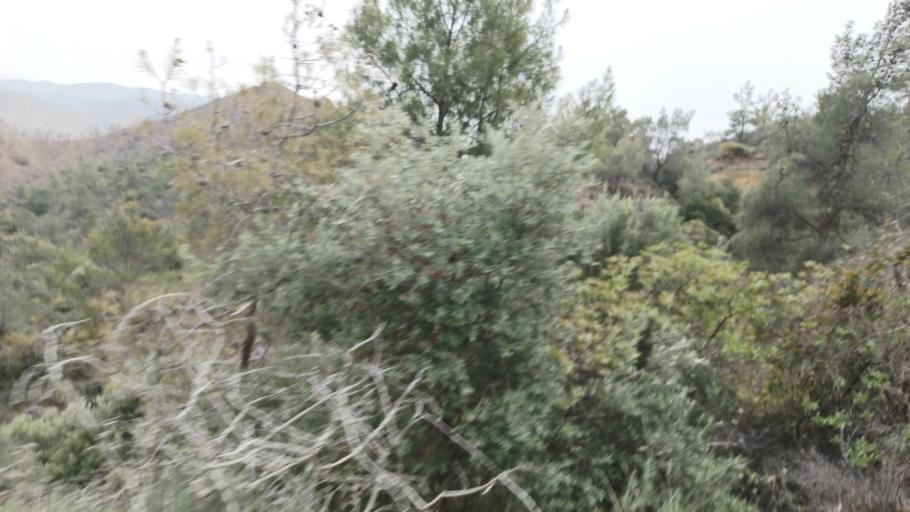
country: CY
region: Limassol
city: Parekklisha
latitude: 34.8569
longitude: 33.1084
